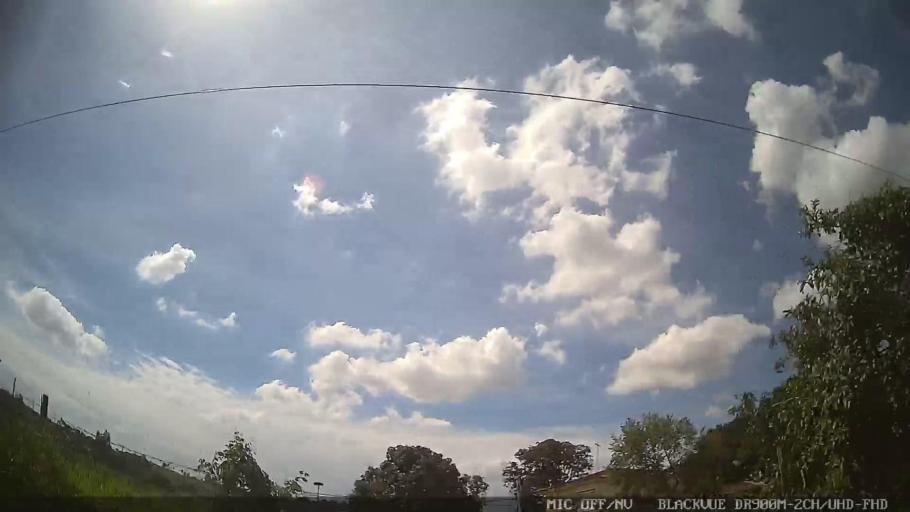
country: BR
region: Sao Paulo
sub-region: Artur Nogueira
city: Artur Nogueira
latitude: -22.6029
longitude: -47.0989
